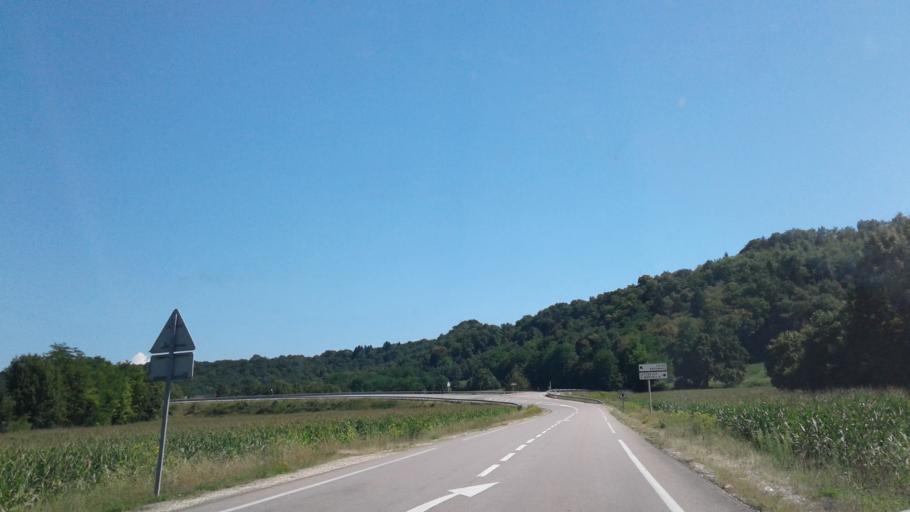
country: FR
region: Rhone-Alpes
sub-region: Departement de l'Ain
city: Artemare
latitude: 45.8628
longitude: 5.6761
